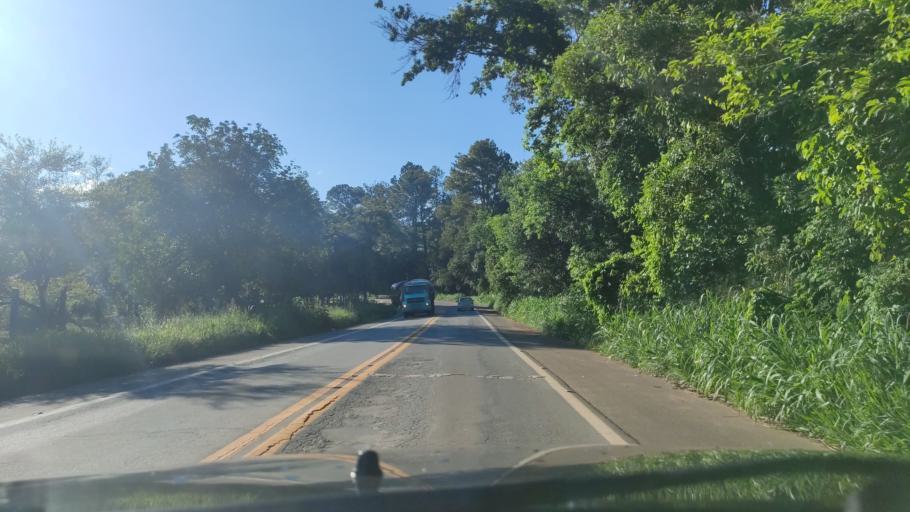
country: BR
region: Sao Paulo
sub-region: Socorro
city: Socorro
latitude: -22.5644
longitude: -46.5406
